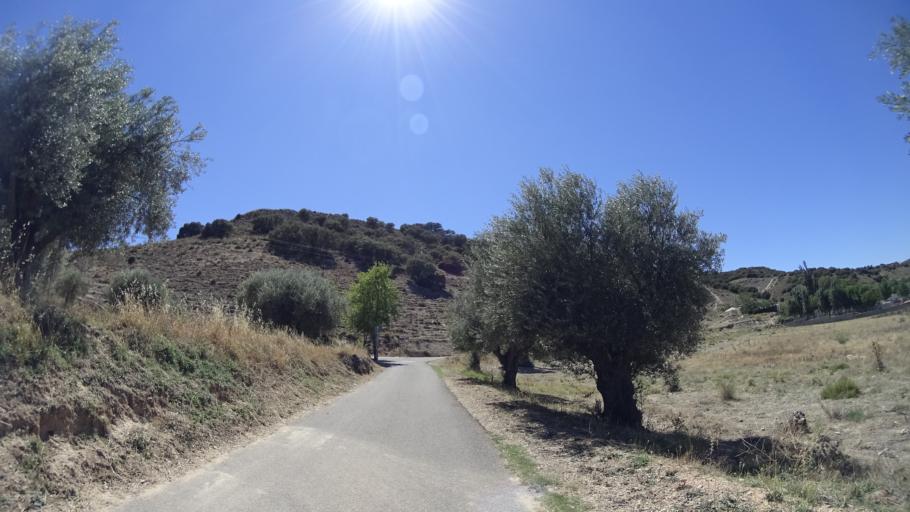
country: ES
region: Madrid
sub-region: Provincia de Madrid
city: Perales de Tajuna
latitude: 40.2235
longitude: -3.3455
